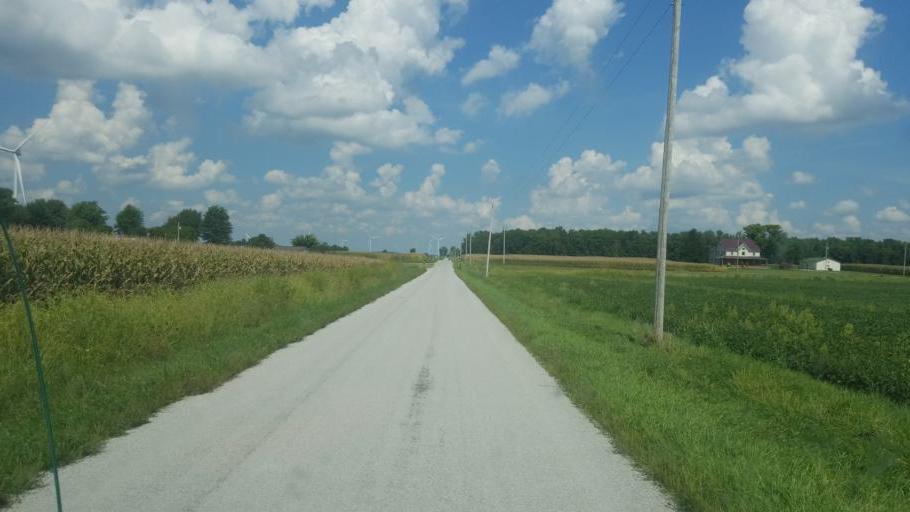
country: US
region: Ohio
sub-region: Hardin County
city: Ada
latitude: 40.7599
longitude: -83.7096
